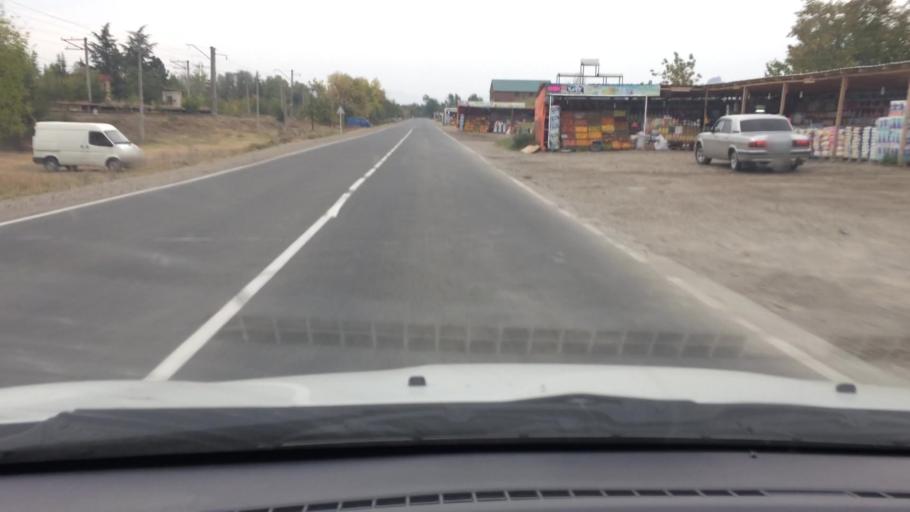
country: GE
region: Kvemo Kartli
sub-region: Marneuli
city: Marneuli
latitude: 41.4214
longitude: 44.8247
